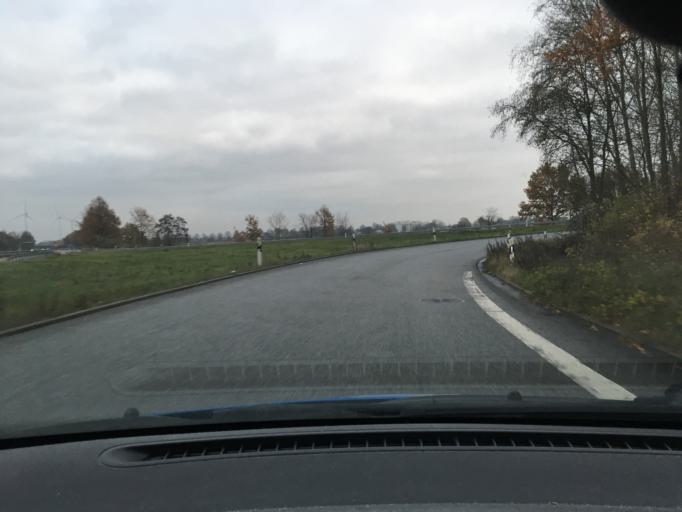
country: DE
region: Hamburg
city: Bergedorf
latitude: 53.4735
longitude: 10.1776
